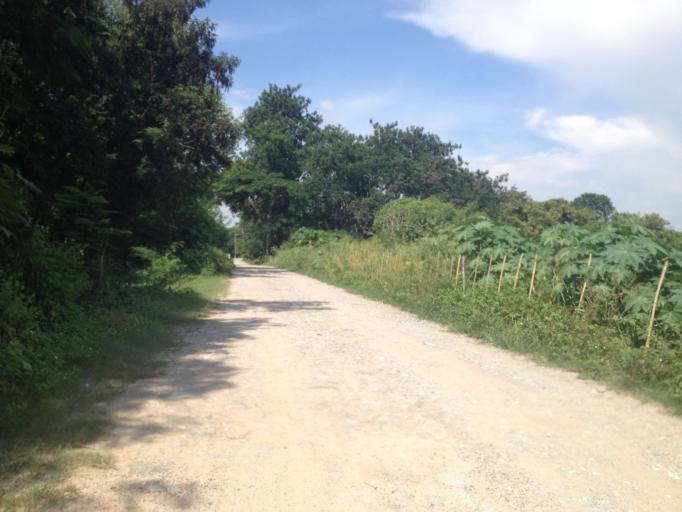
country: TH
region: Chiang Mai
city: Chiang Mai
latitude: 18.7556
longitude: 98.9434
